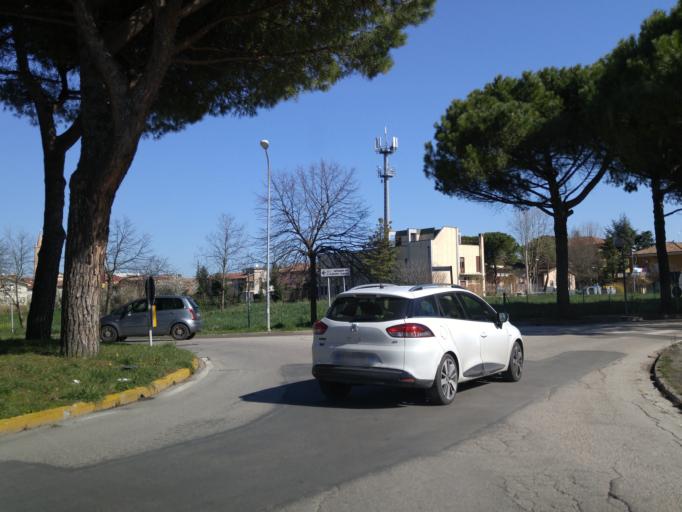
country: IT
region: Emilia-Romagna
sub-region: Provincia di Rimini
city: Cattolica
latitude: 43.9595
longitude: 12.7403
